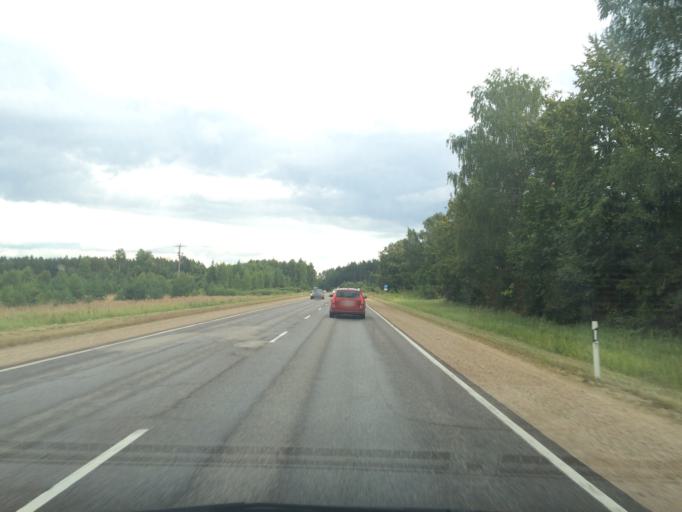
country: LV
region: Koknese
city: Koknese
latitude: 56.5902
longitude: 25.5587
